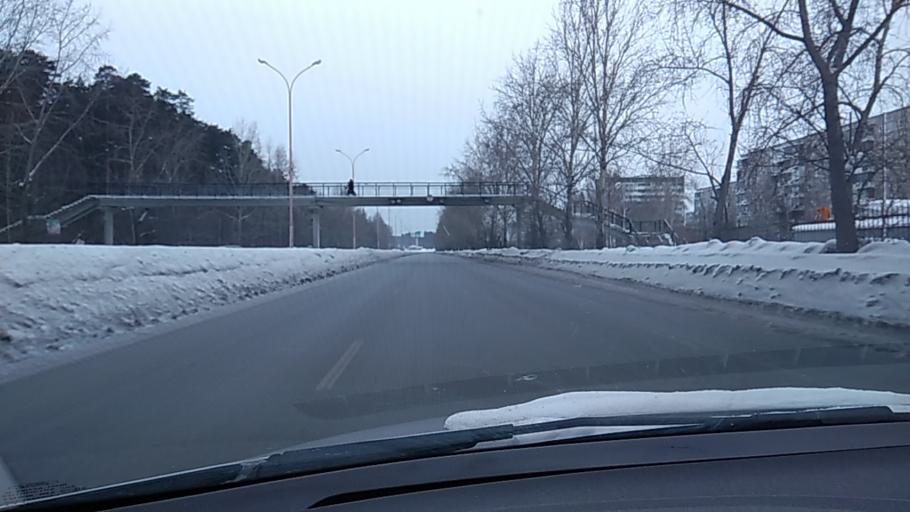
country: RU
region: Sverdlovsk
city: Sovkhoznyy
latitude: 56.7975
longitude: 60.5577
